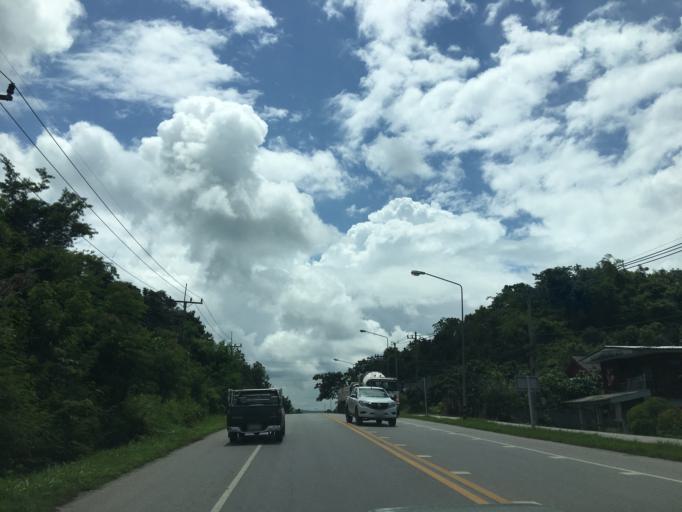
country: TH
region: Chiang Rai
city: Pa Daet
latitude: 19.6551
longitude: 99.9349
